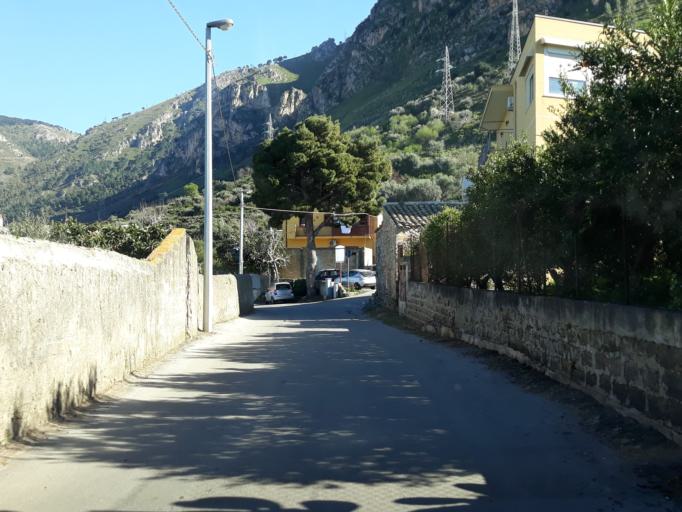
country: IT
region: Sicily
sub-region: Palermo
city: Villa Ciambra
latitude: 38.0760
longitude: 13.3493
